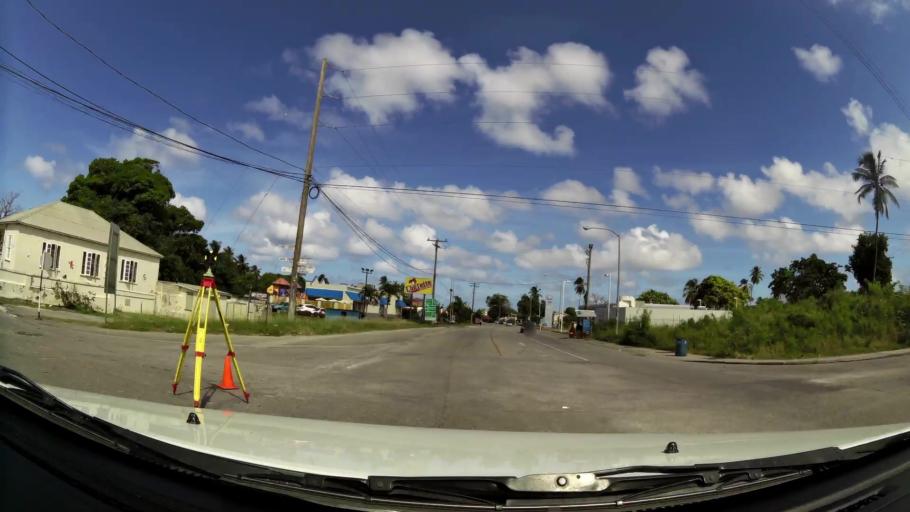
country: BB
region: Saint Peter
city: Speightstown
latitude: 13.2491
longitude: -59.6416
